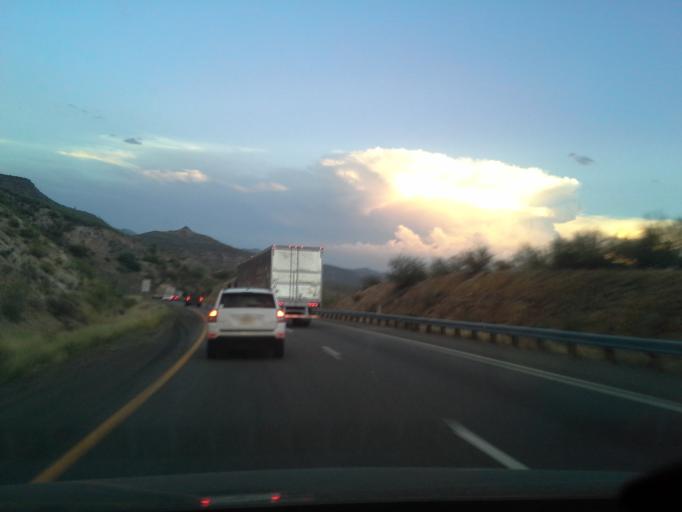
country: US
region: Arizona
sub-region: Yavapai County
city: Black Canyon City
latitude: 34.1146
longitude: -112.1462
